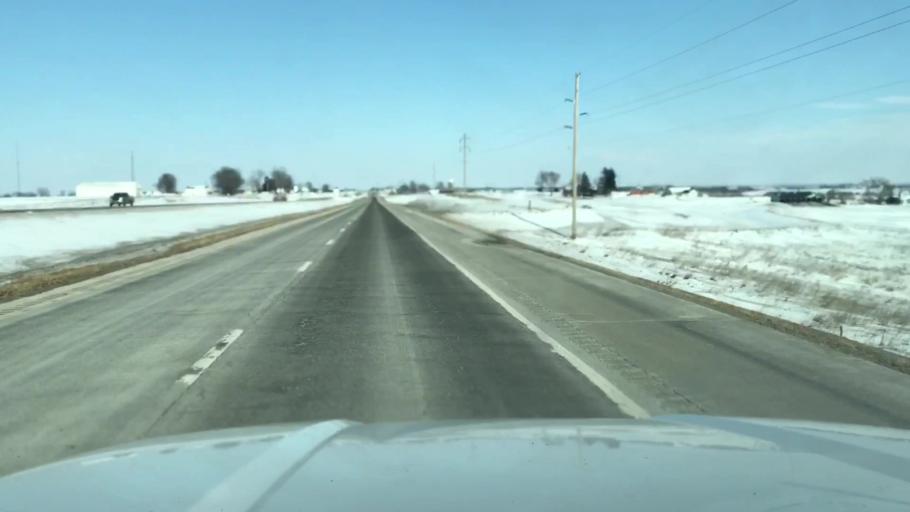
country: US
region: Missouri
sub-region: Nodaway County
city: Maryville
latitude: 40.2341
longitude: -94.8675
